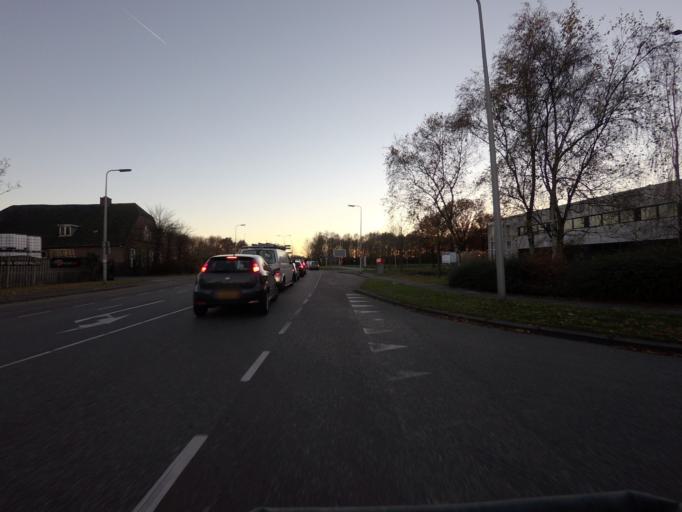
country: NL
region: Utrecht
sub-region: Gemeente Nieuwegein
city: Nieuwegein
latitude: 52.0713
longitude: 5.0543
